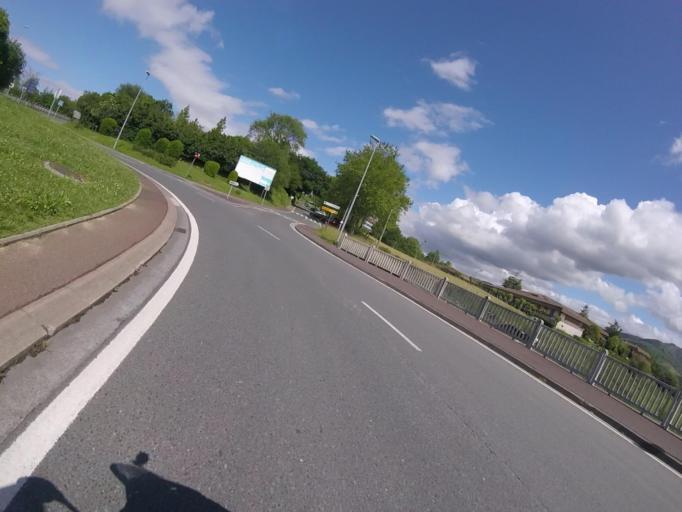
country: ES
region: Basque Country
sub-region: Provincia de Guipuzcoa
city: Errenteria
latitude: 43.2915
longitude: -1.9009
